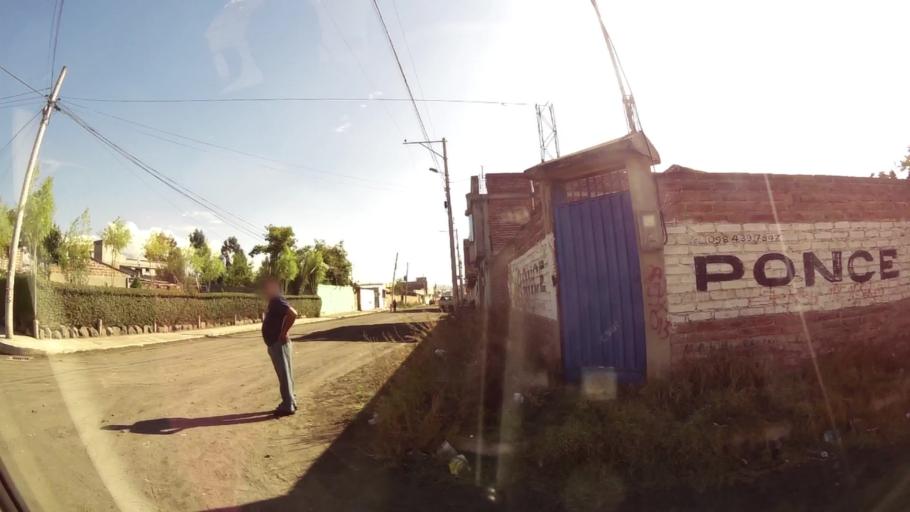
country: EC
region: Chimborazo
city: Riobamba
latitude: -1.6494
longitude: -78.6751
